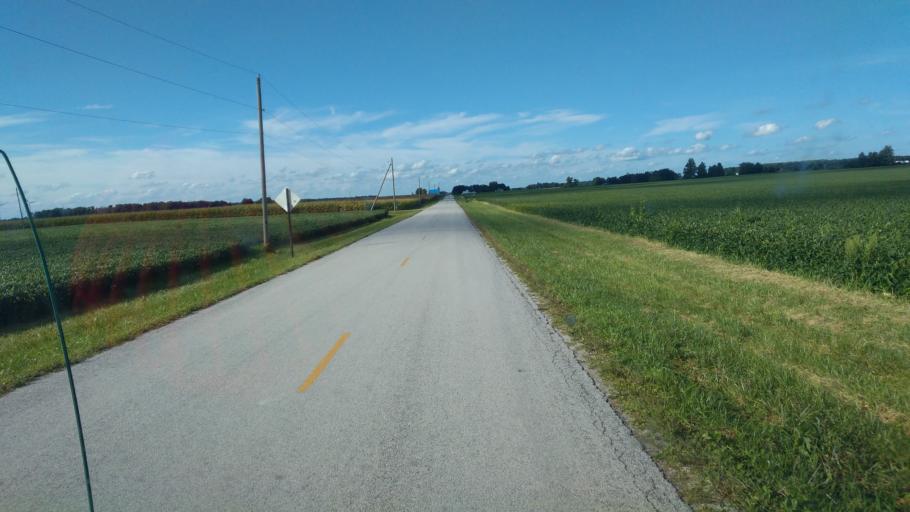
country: US
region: Ohio
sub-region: Hardin County
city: Kenton
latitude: 40.7343
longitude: -83.6908
